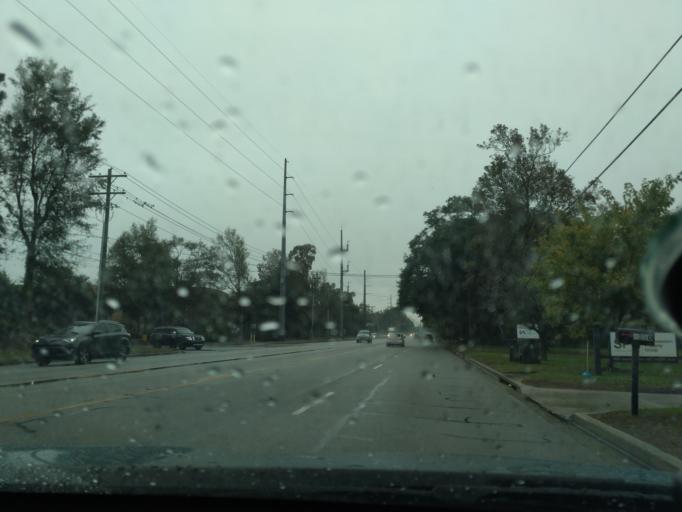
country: US
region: South Carolina
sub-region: Charleston County
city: Charleston
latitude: 32.7198
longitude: -79.9662
